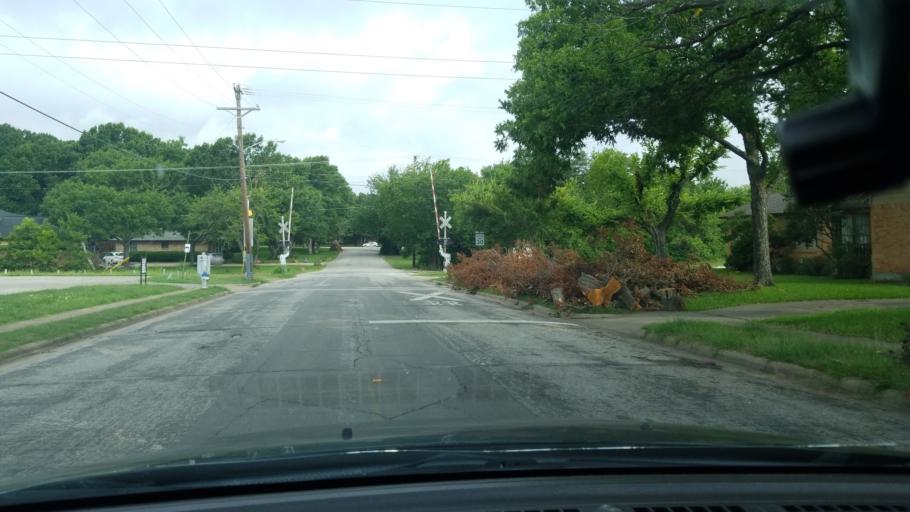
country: US
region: Texas
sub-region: Dallas County
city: Highland Park
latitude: 32.8266
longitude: -96.6935
